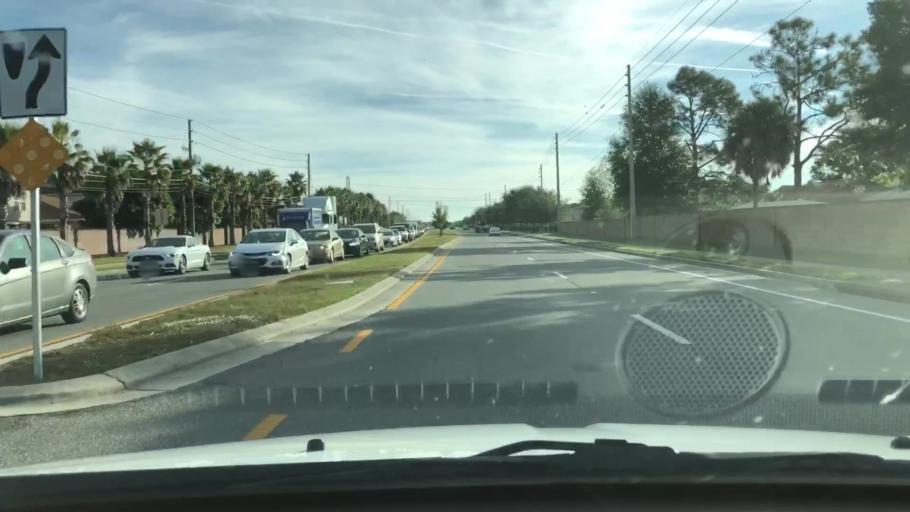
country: US
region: Florida
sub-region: Orange County
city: Meadow Woods
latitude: 28.3923
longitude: -81.3604
